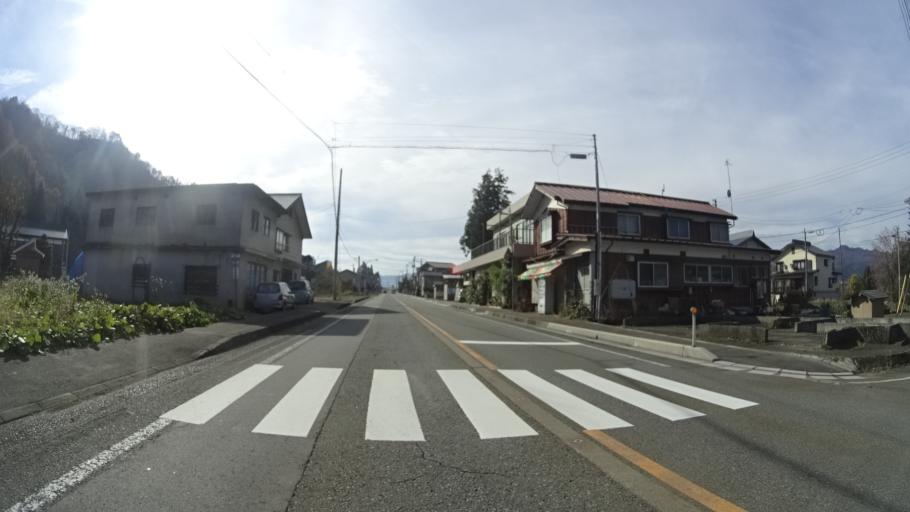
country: JP
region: Niigata
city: Muikamachi
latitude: 37.1216
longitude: 138.9258
